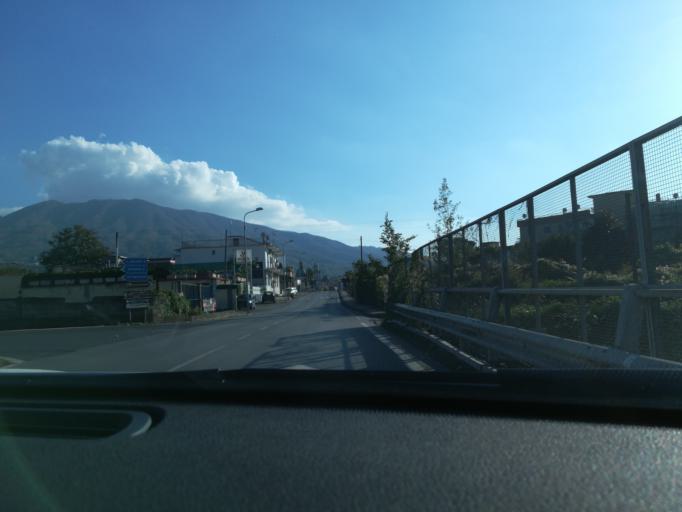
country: IT
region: Campania
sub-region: Provincia di Napoli
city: Sant'Anastasia
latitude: 40.8752
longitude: 14.3865
